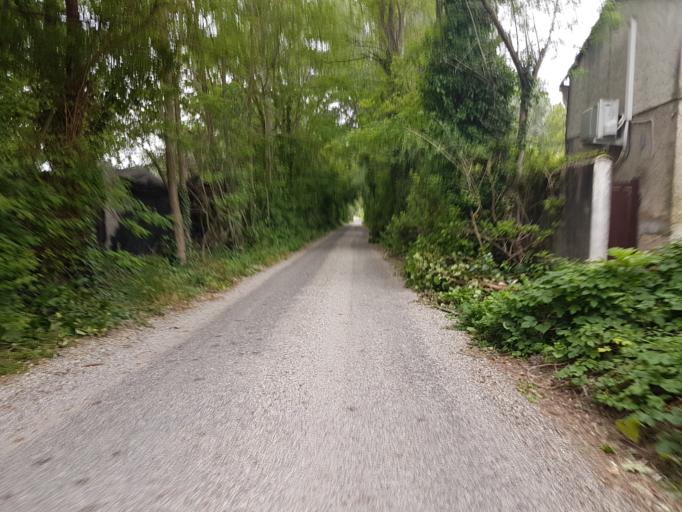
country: FR
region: Languedoc-Roussillon
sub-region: Departement du Gard
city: Roquemaure
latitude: 44.0381
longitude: 4.7822
